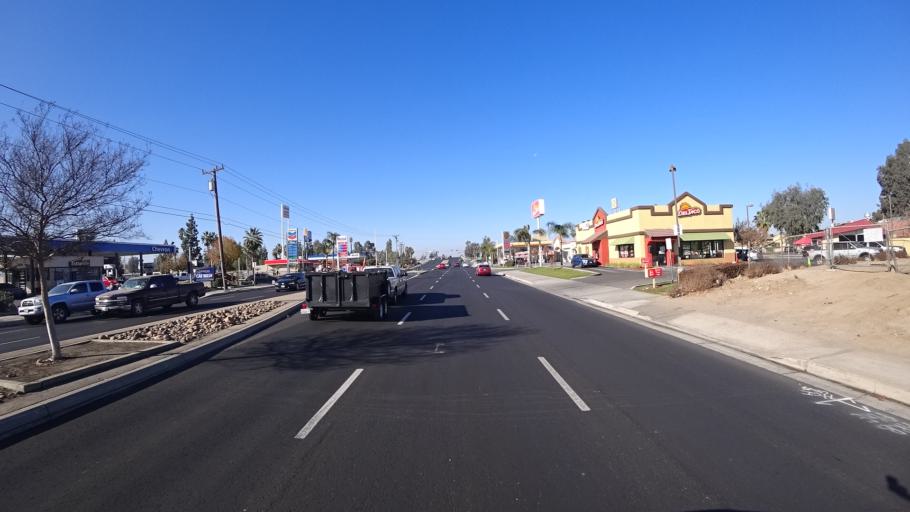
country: US
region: California
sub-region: Kern County
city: Greenfield
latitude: 35.3177
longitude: -119.0316
